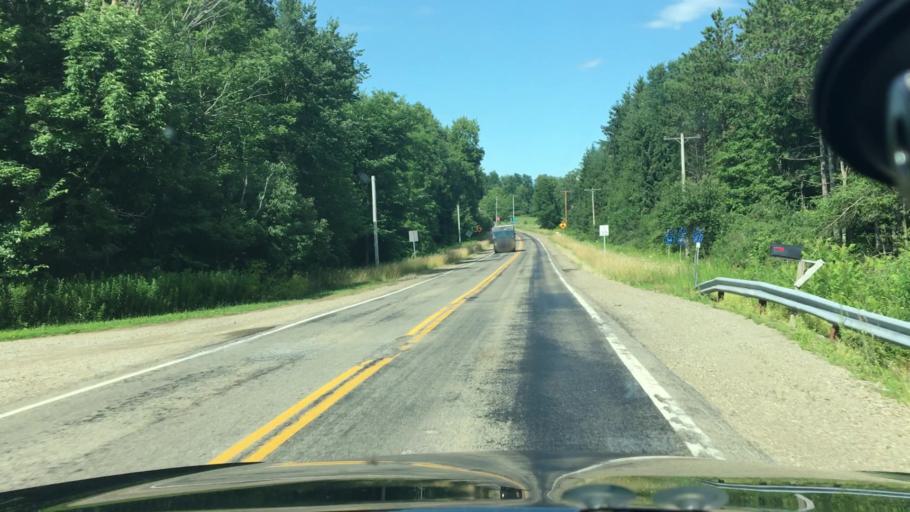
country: US
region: New York
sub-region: Chautauqua County
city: Lakewood
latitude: 42.2565
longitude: -79.3504
